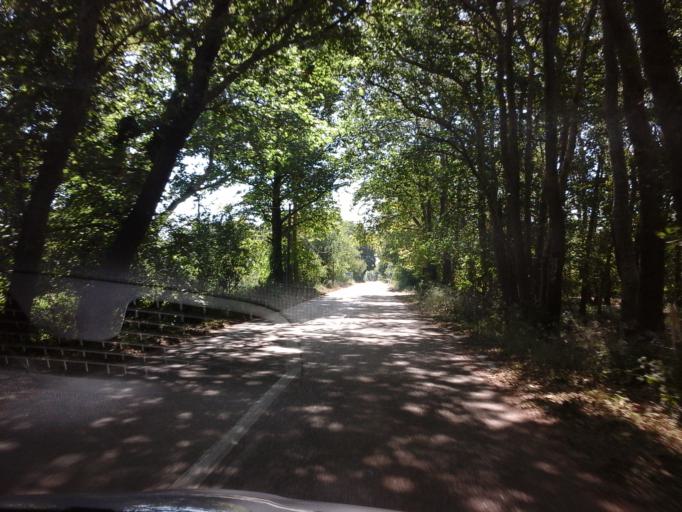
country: GR
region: East Macedonia and Thrace
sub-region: Nomos Evrou
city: Samothraki
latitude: 40.5083
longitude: 25.5720
